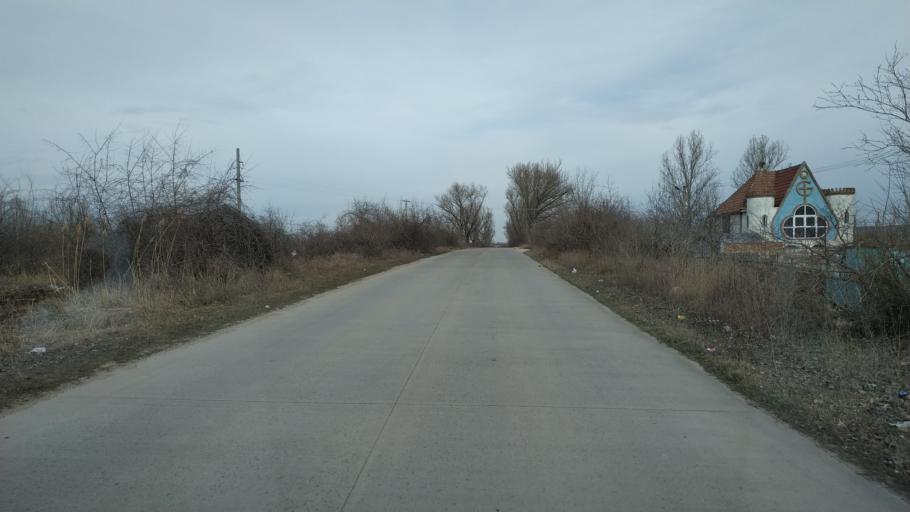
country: MD
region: Chisinau
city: Vatra
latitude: 47.0957
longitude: 28.7352
